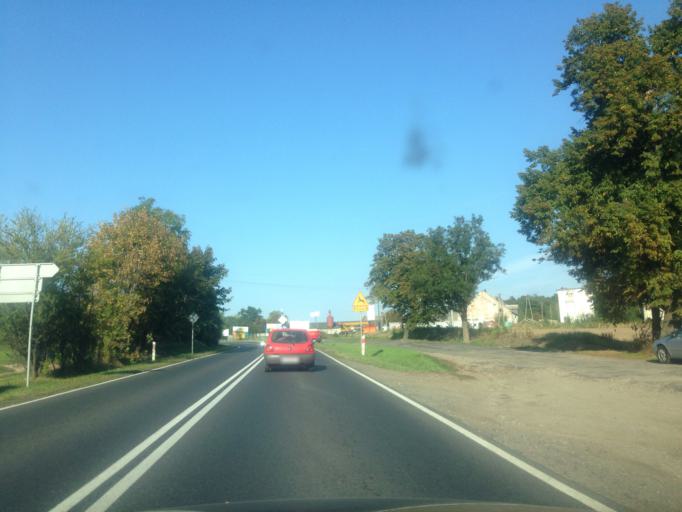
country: PL
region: Kujawsko-Pomorskie
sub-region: Powiat brodnicki
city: Brzozie
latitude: 53.2961
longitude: 19.5028
